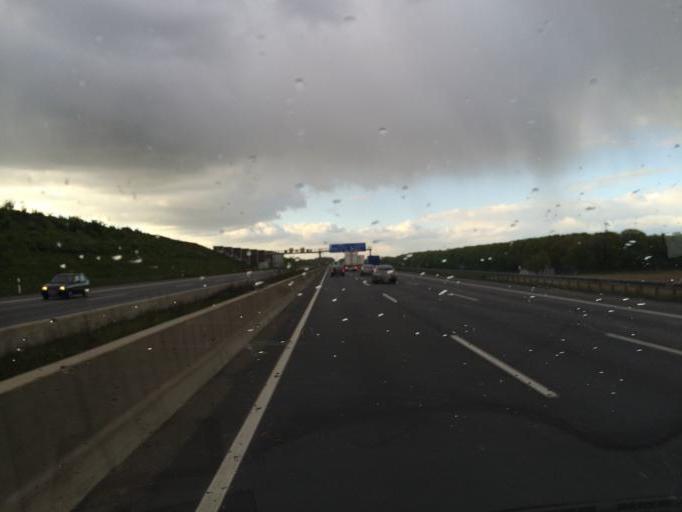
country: DE
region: North Rhine-Westphalia
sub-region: Regierungsbezirk Koln
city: Mengenich
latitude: 50.9665
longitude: 6.8506
